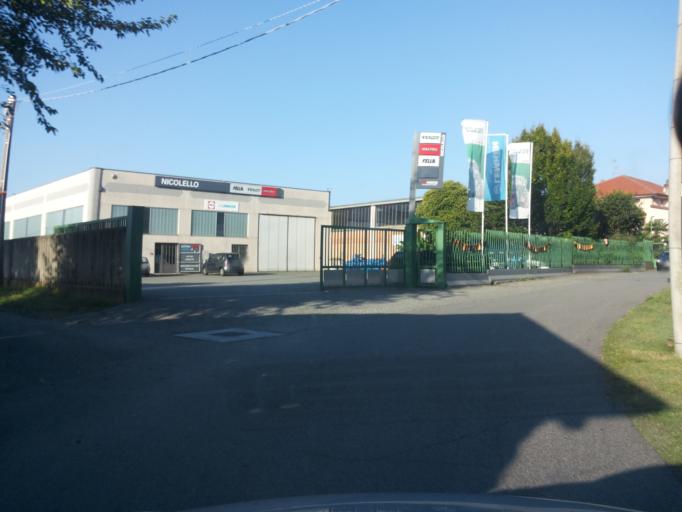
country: IT
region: Piedmont
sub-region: Provincia di Biella
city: Cavaglia
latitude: 45.4023
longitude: 8.0876
